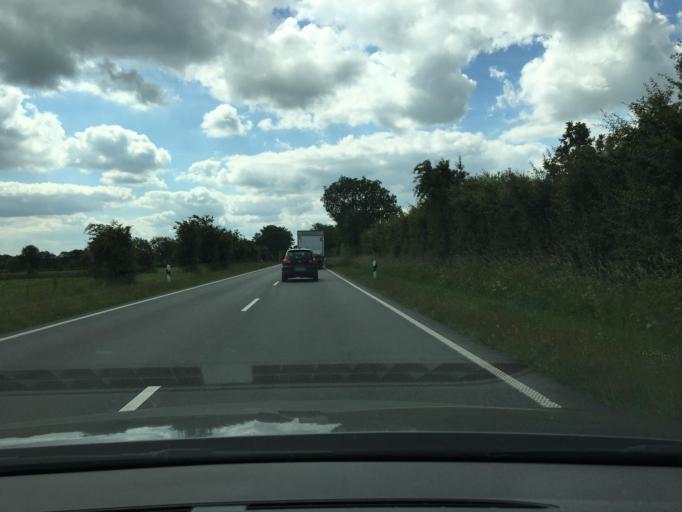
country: DE
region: Schleswig-Holstein
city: Klein Rheide
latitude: 54.4358
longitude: 9.4855
